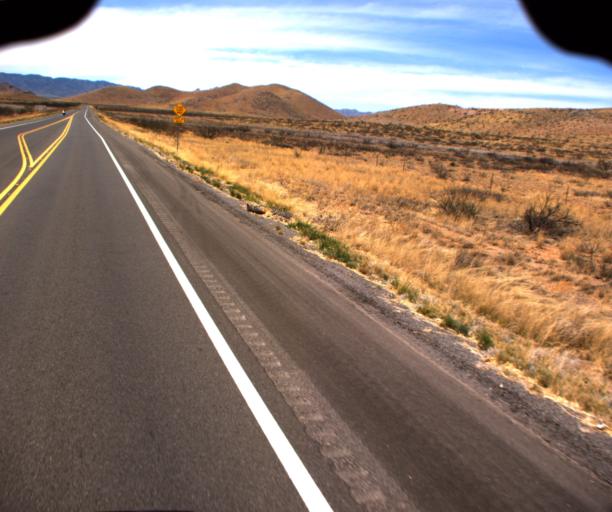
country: US
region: Arizona
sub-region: Cochise County
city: Willcox
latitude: 31.9055
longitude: -109.7645
